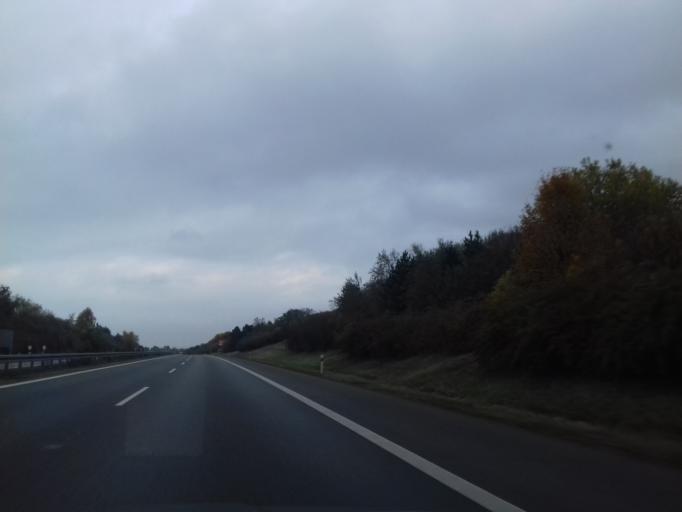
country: CZ
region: South Moravian
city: Kostice
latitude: 48.7354
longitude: 16.9768
